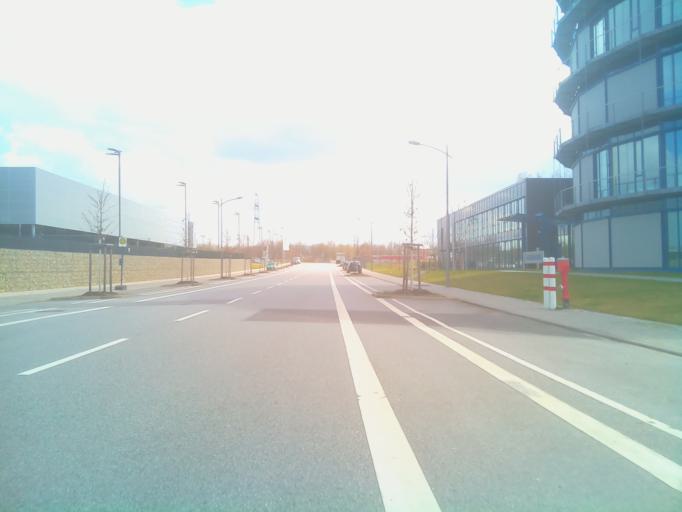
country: DE
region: Baden-Wuerttemberg
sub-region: Karlsruhe Region
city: Ilvesheim
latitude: 49.4504
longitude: 8.5647
